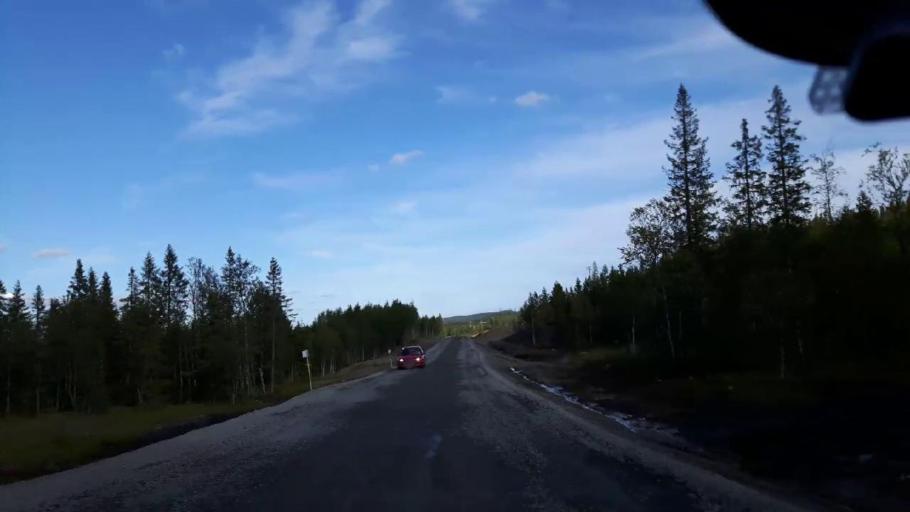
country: SE
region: Jaemtland
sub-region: Ragunda Kommun
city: Hammarstrand
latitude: 63.4250
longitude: 16.1294
